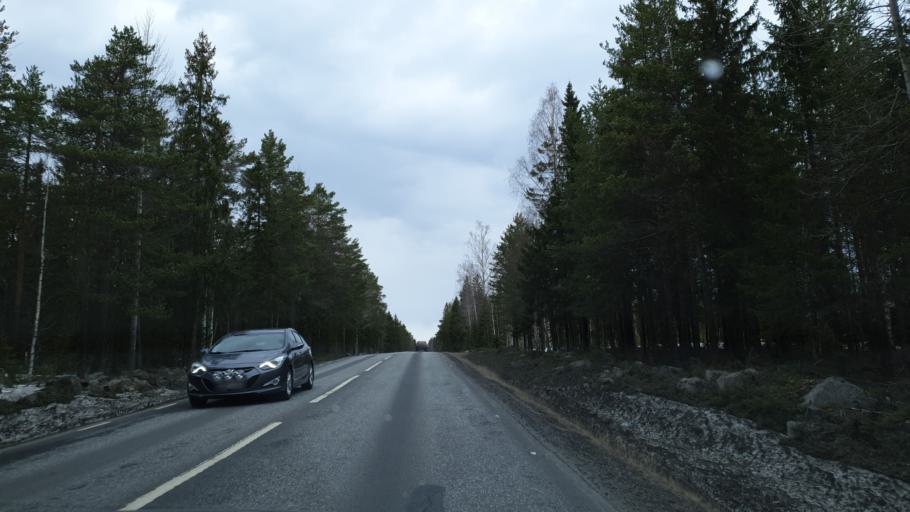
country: SE
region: Vaesterbotten
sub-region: Skelleftea Kommun
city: Viken
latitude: 64.6554
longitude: 20.9540
